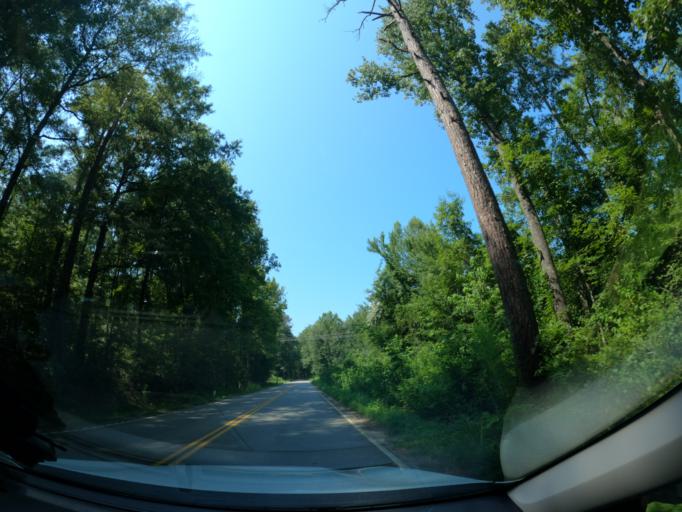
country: US
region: South Carolina
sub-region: Richland County
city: Hopkins
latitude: 33.8574
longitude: -80.8779
